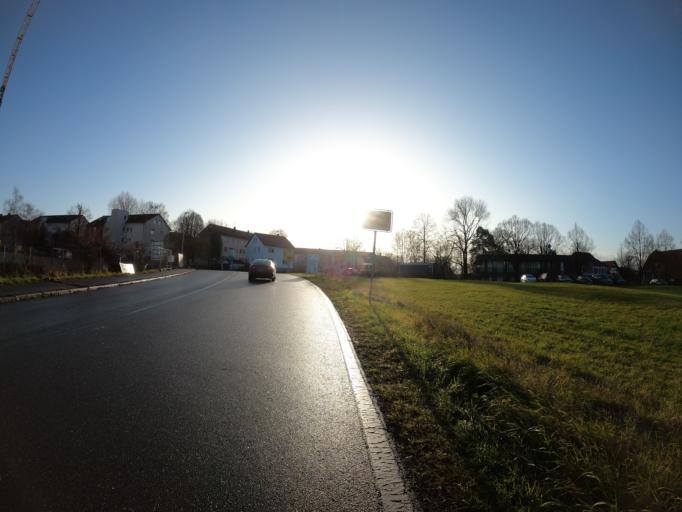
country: DE
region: Baden-Wuerttemberg
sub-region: Regierungsbezirk Stuttgart
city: Goeppingen
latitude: 48.6891
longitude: 9.6270
